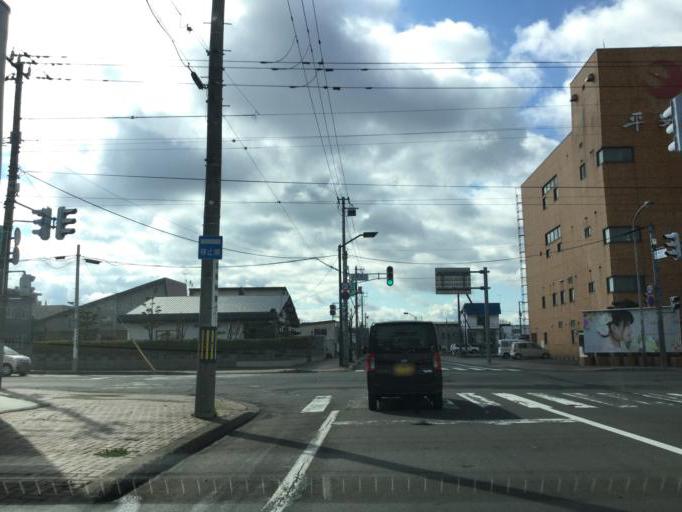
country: JP
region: Hokkaido
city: Iwamizawa
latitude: 43.2048
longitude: 141.7685
